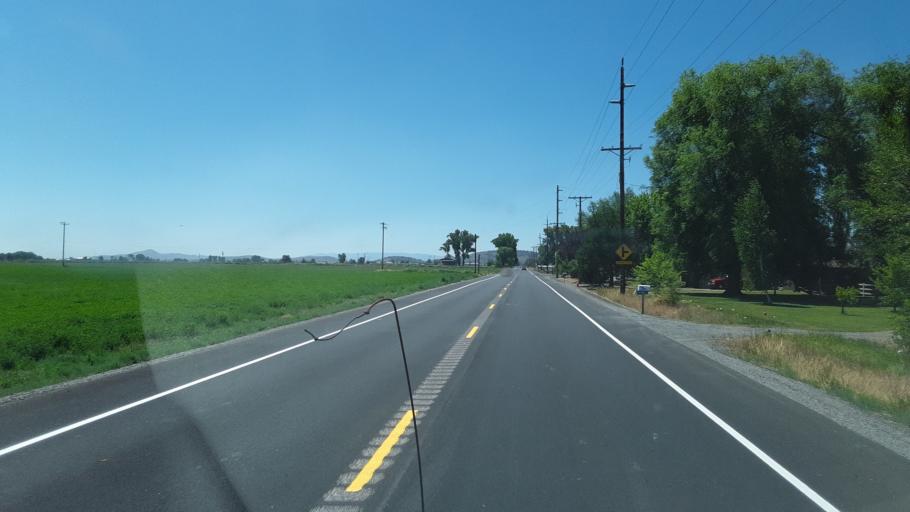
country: US
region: Oregon
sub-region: Klamath County
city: Altamont
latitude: 42.1278
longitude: -121.6985
